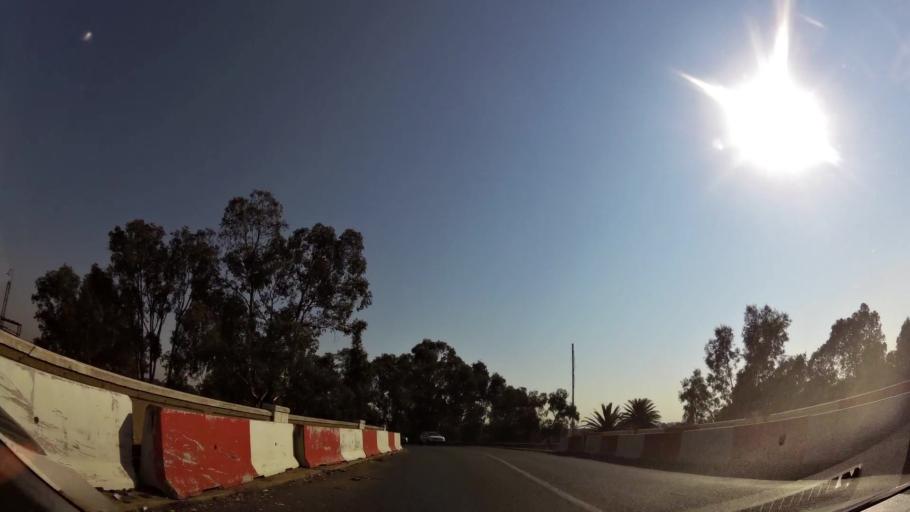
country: ZA
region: Gauteng
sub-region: Ekurhuleni Metropolitan Municipality
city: Boksburg
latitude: -26.2170
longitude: 28.2636
